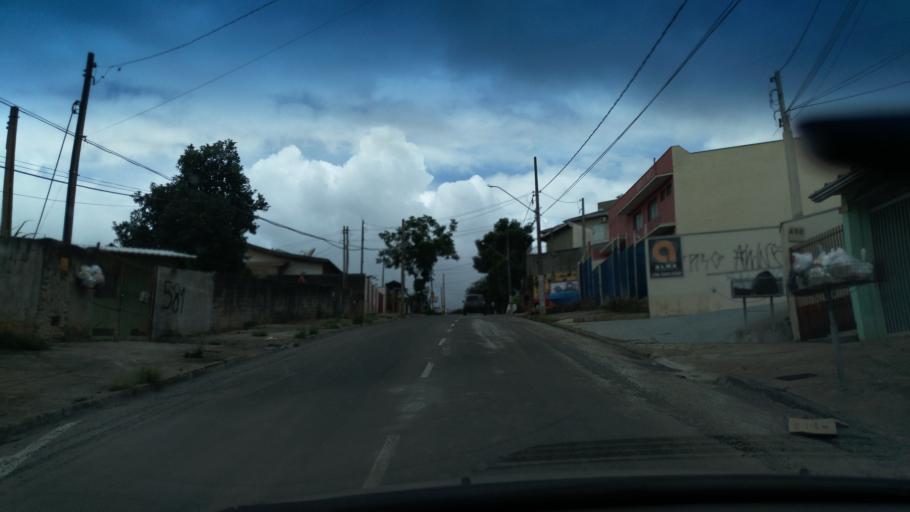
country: BR
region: Sao Paulo
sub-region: Valinhos
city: Valinhos
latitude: -22.9581
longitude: -47.0017
